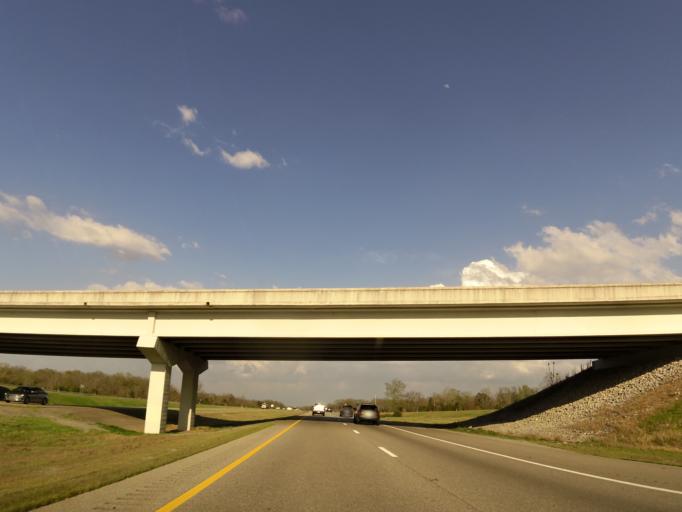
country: US
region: Tennessee
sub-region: Williamson County
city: Nolensville
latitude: 35.8587
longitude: -86.5801
